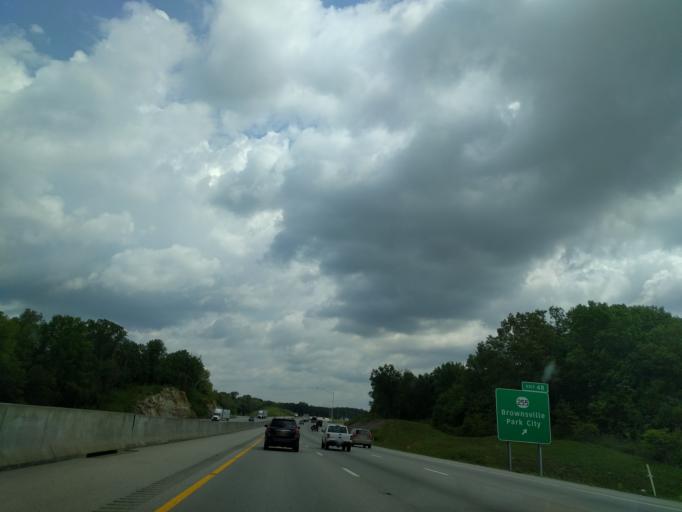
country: US
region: Kentucky
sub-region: Barren County
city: Cave City
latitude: 37.0929
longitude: -86.0588
